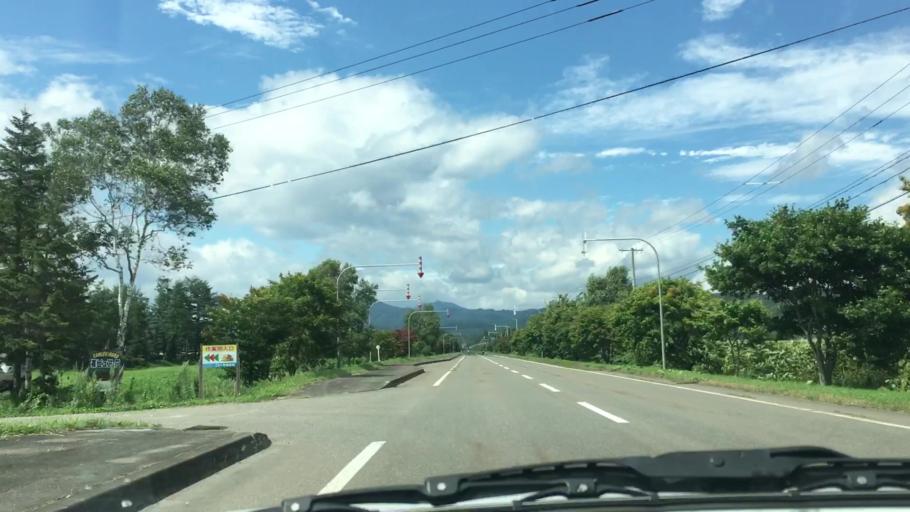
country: JP
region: Hokkaido
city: Otofuke
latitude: 43.3093
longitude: 143.3091
